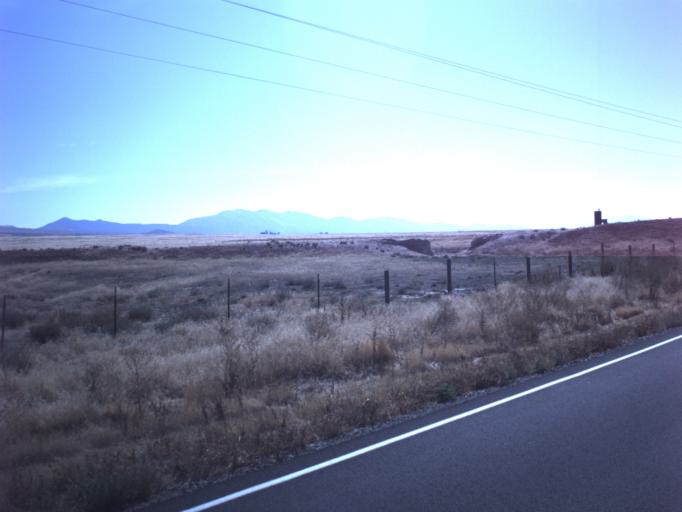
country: US
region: Utah
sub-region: Tooele County
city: Grantsville
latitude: 40.4245
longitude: -112.7488
